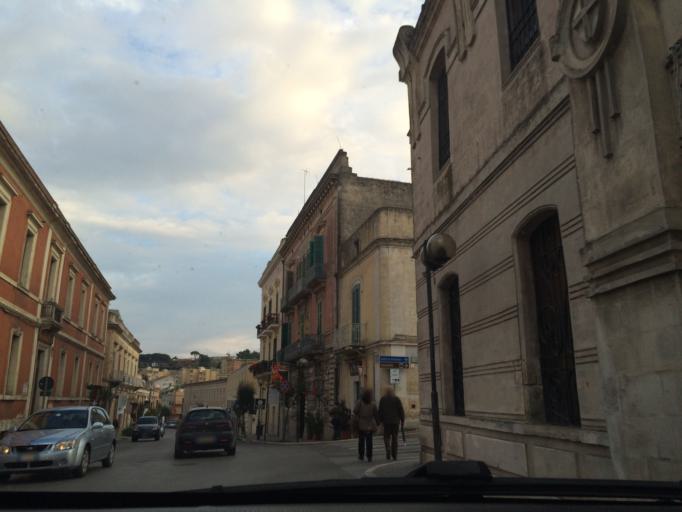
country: IT
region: Basilicate
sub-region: Provincia di Matera
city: Matera
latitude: 40.6639
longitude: 16.6079
